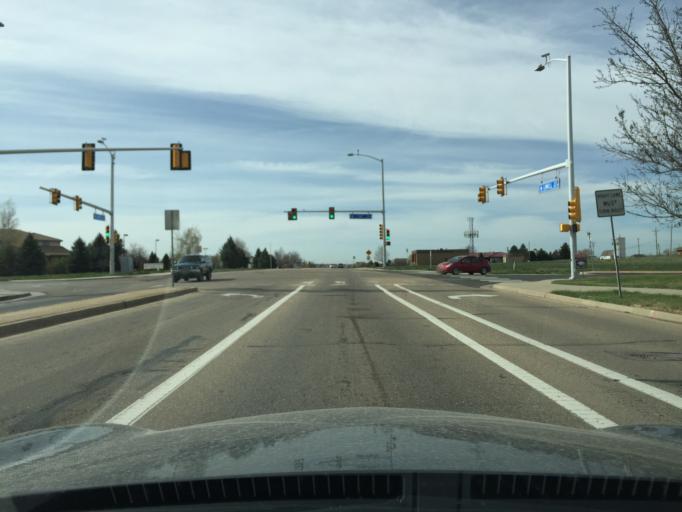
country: US
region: Colorado
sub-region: Broomfield County
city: Broomfield
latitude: 39.9437
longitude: -105.0344
